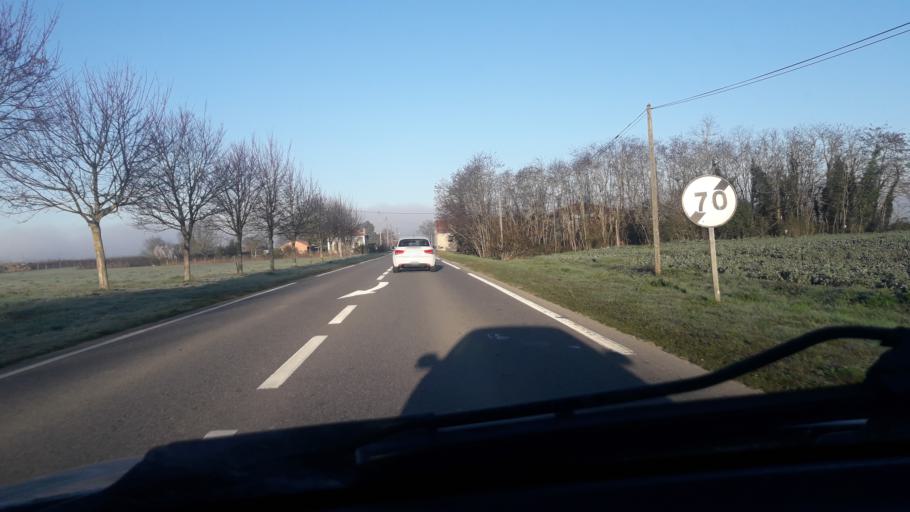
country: FR
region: Midi-Pyrenees
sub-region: Departement de la Haute-Garonne
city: Carbonne
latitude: 43.2975
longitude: 1.1985
